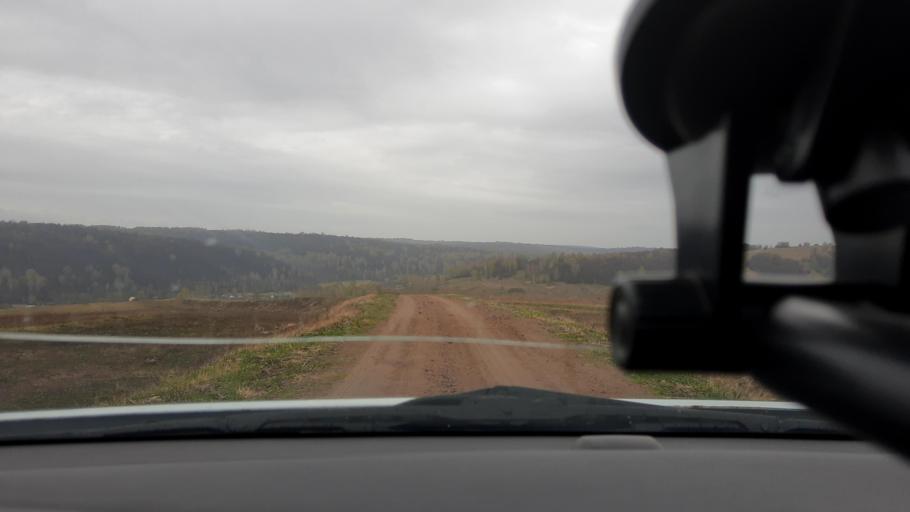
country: RU
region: Bashkortostan
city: Pavlovka
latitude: 55.4315
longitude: 56.3189
